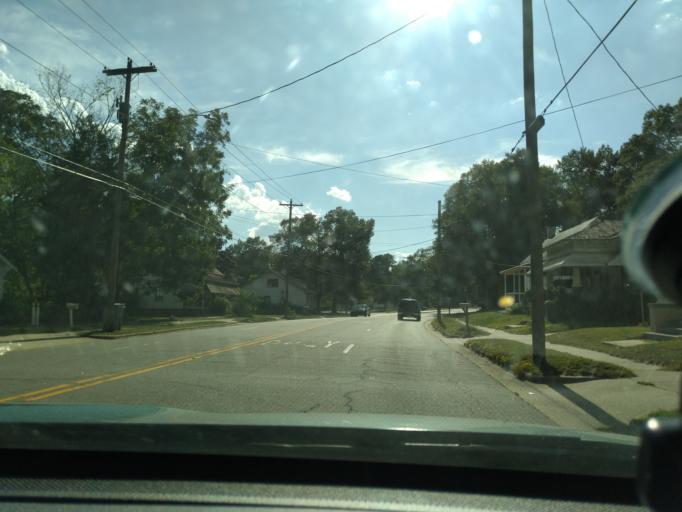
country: US
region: North Carolina
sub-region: Nash County
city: Rocky Mount
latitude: 35.9371
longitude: -77.7936
